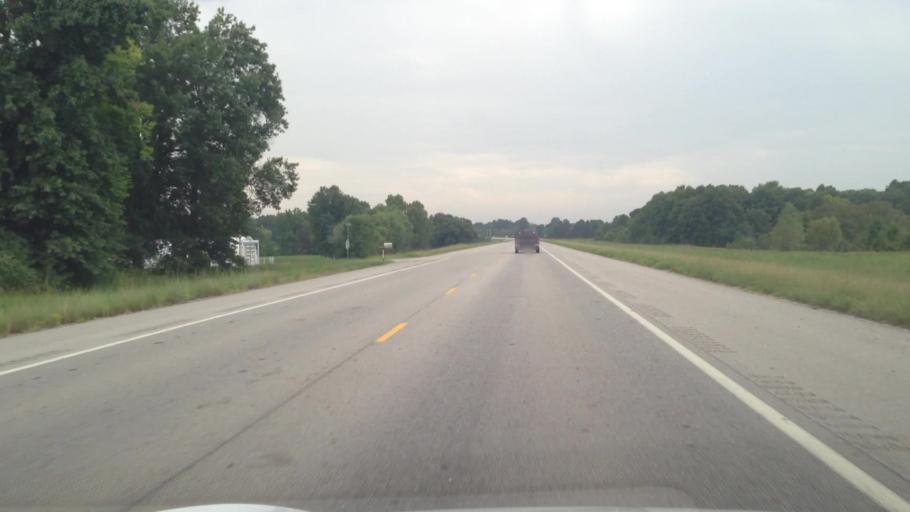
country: US
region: Kansas
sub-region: Cherokee County
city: Baxter Springs
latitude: 37.0656
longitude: -94.7269
